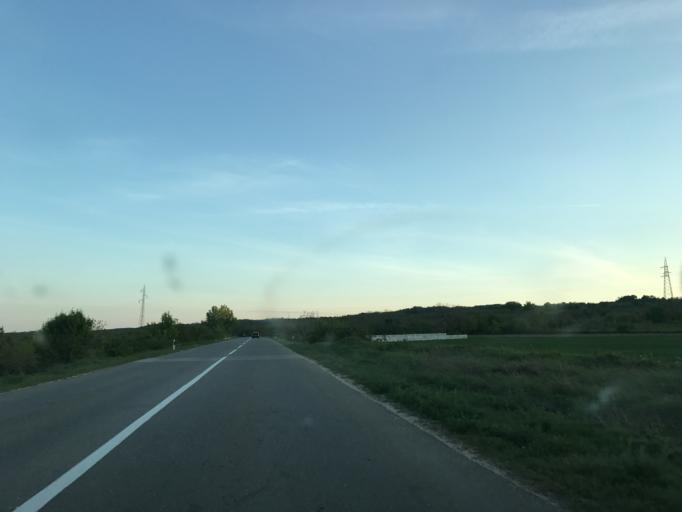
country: RO
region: Mehedinti
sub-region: Comuna Gogosu
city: Ostrovu Mare
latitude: 44.3444
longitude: 22.4744
